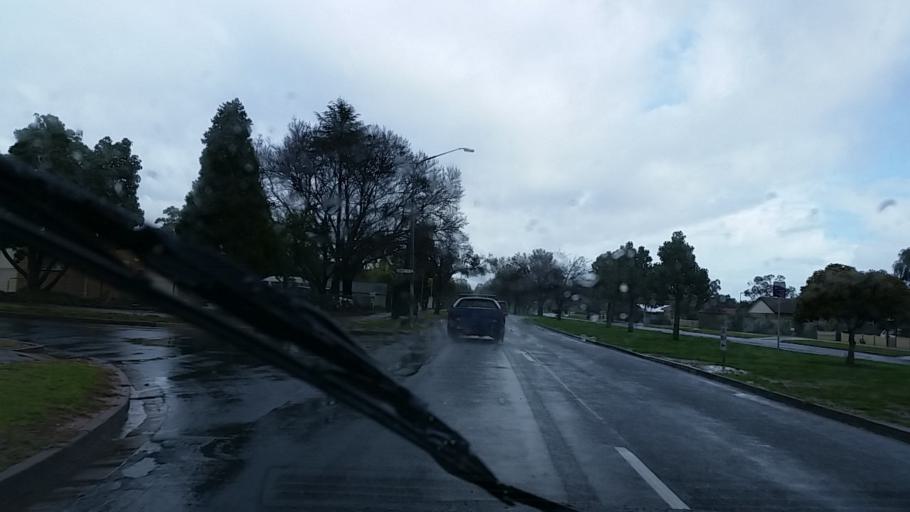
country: AU
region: South Australia
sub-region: Salisbury
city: Elizabeth
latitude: -34.7121
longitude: 138.6828
